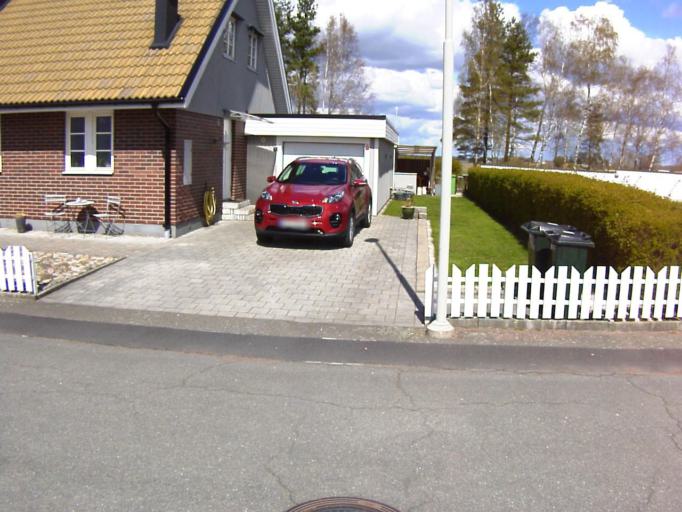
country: SE
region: Skane
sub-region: Kristianstads Kommun
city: Kristianstad
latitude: 56.0158
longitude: 14.1002
